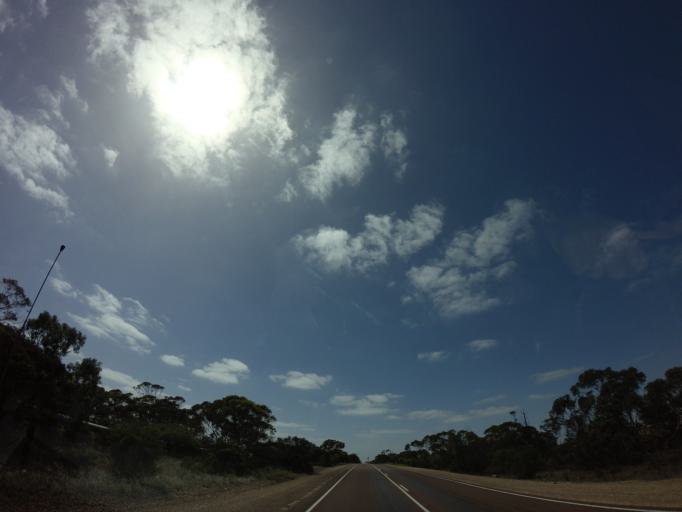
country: AU
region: South Australia
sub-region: Kimba
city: Caralue
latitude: -33.1235
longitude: 135.5439
